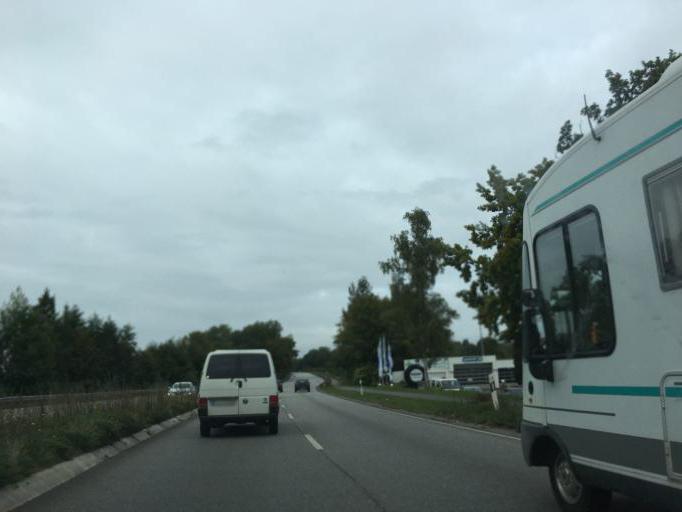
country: DE
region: Schleswig-Holstein
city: Windeby
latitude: 54.4725
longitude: 9.8259
